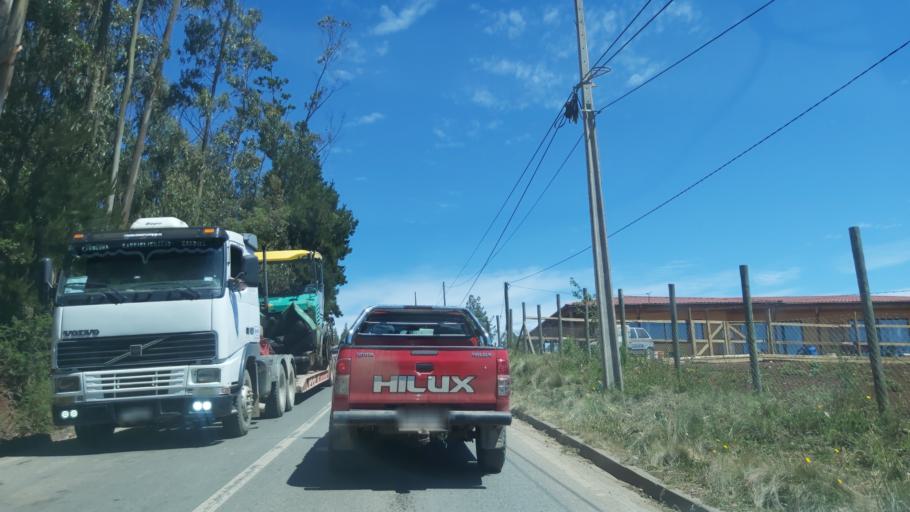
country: CL
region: Maule
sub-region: Provincia de Talca
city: Constitucion
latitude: -35.3888
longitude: -72.4240
